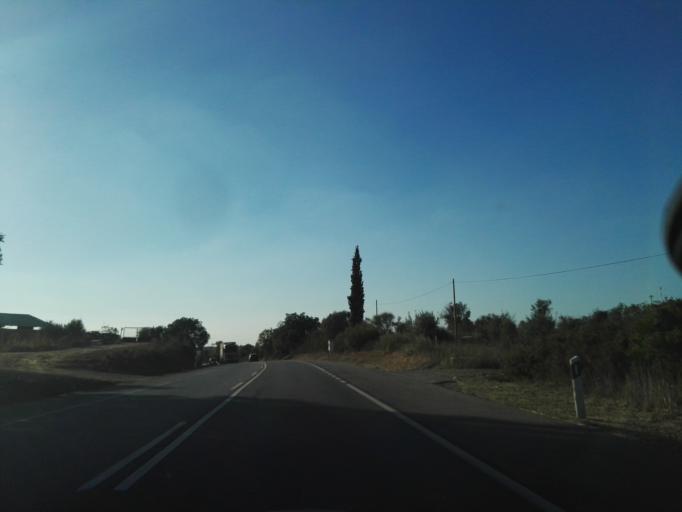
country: PT
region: Evora
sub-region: Estremoz
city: Estremoz
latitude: 38.8360
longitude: -7.5696
